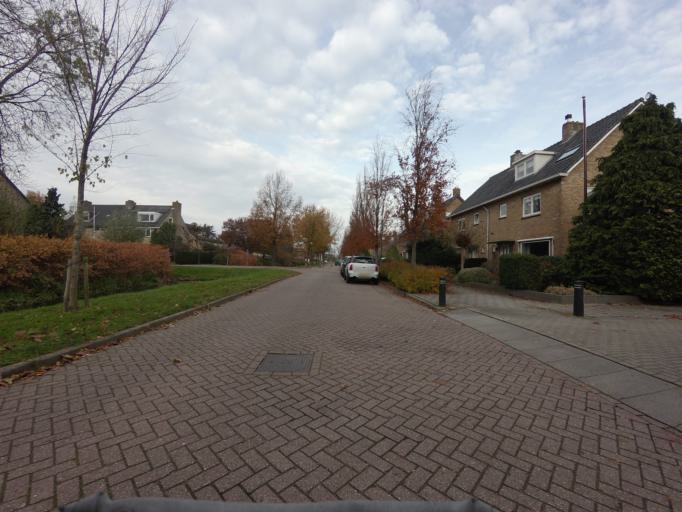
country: NL
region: North Holland
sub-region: Gemeente Amsterdam
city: Amsterdam-Zuidoost
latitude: 52.2718
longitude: 4.9657
